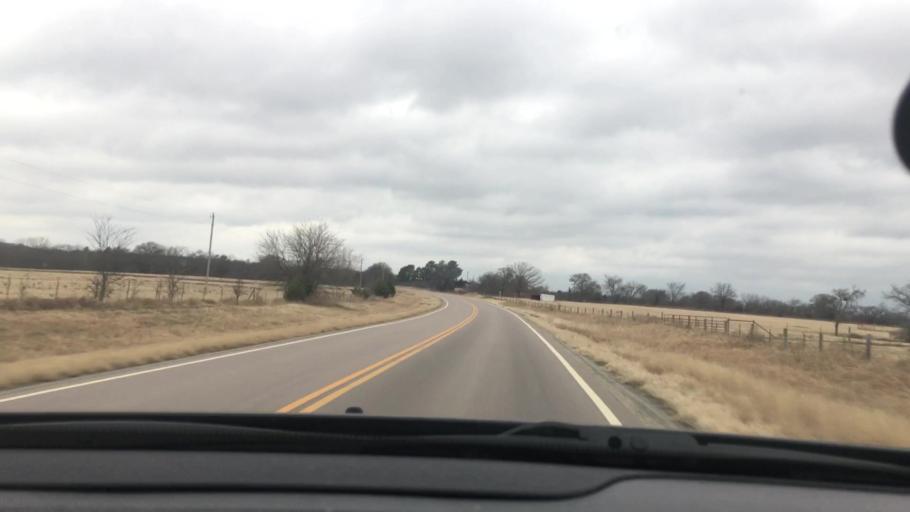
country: US
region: Oklahoma
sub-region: Coal County
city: Coalgate
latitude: 34.3736
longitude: -96.3600
